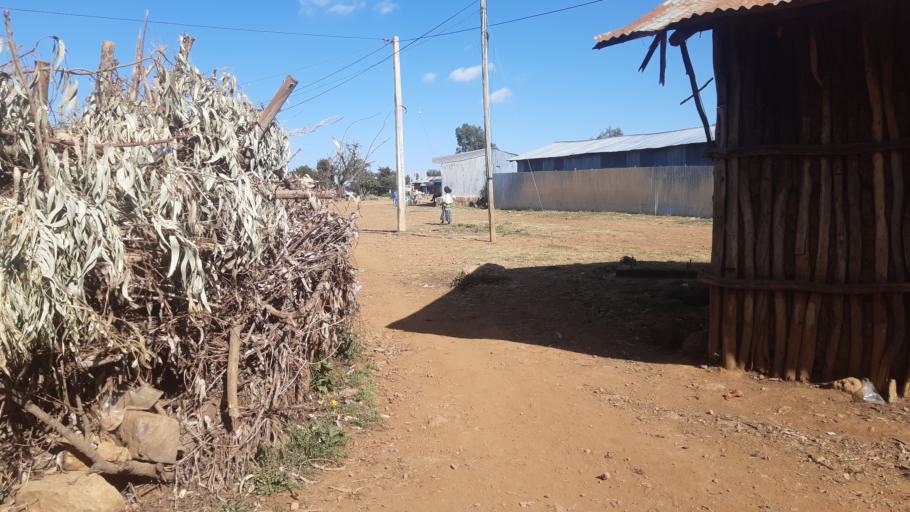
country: ET
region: Amhara
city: Dabat
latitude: 13.3508
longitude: 37.3895
